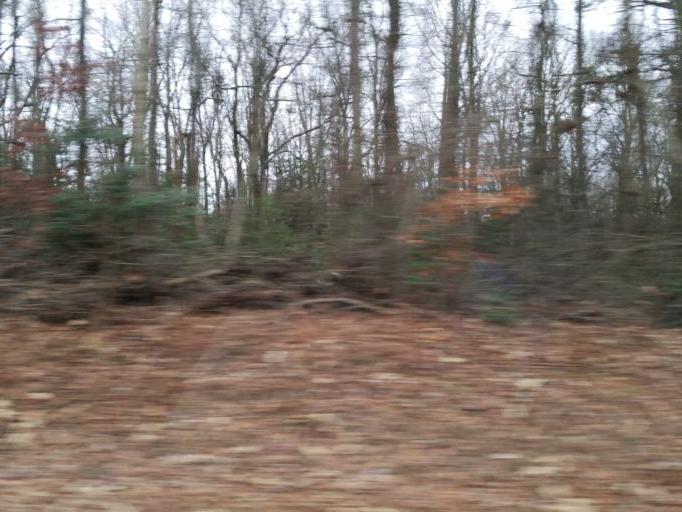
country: US
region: Georgia
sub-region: Dawson County
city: Dawsonville
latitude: 34.4919
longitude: -84.1841
